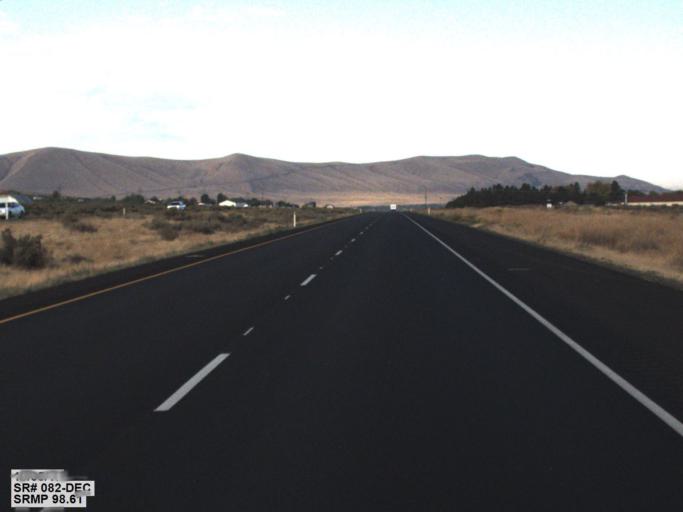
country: US
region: Washington
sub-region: Benton County
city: Benton City
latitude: 46.2585
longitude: -119.4349
